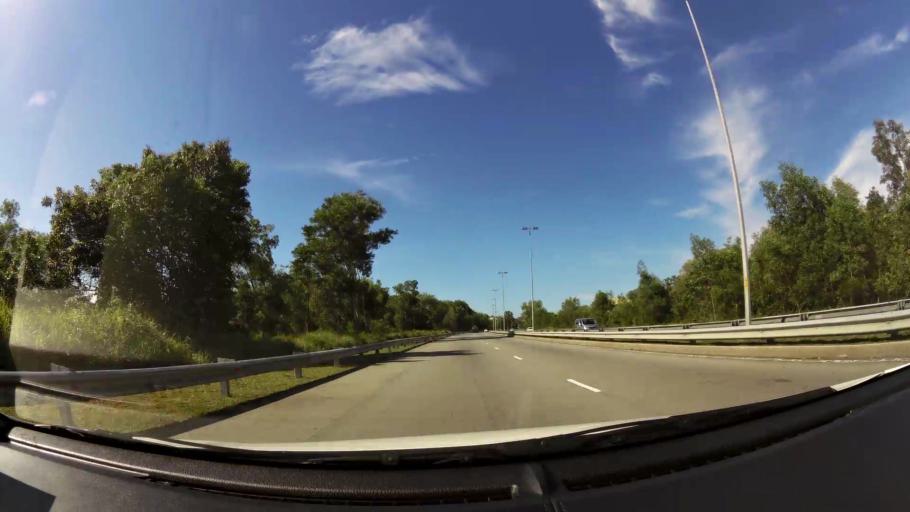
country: BN
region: Brunei and Muara
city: Bandar Seri Begawan
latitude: 4.9681
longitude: 114.9265
